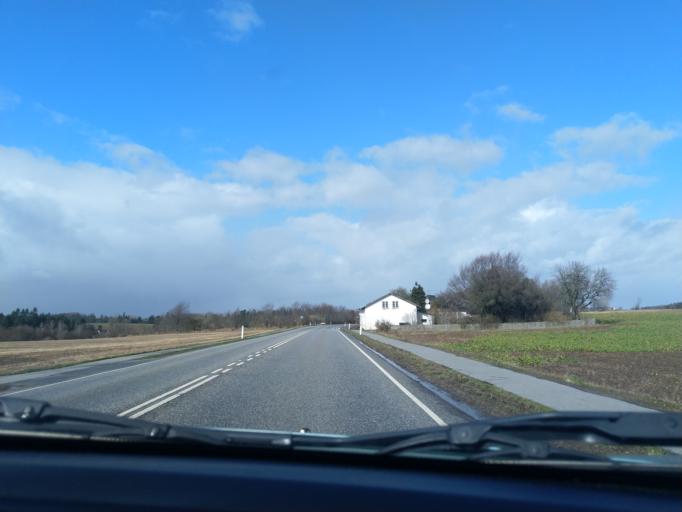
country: DK
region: Zealand
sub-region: Naestved Kommune
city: Naestved
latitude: 55.2966
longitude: 11.6941
